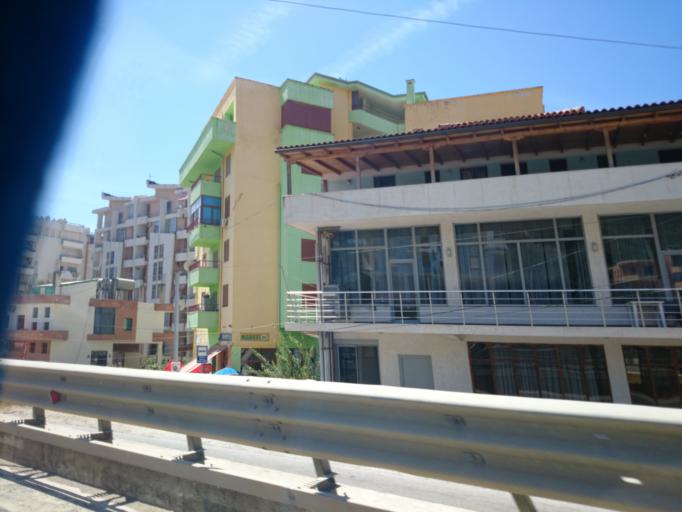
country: AL
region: Tirane
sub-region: Rrethi i Kavajes
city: Golem
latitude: 41.2777
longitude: 19.5149
